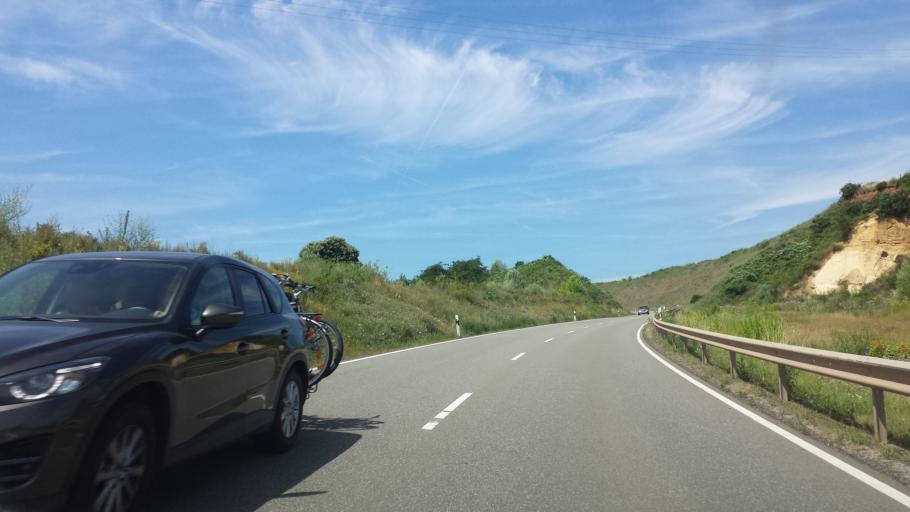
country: DE
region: Rheinland-Pfalz
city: Eisenberg
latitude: 49.5658
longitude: 8.0786
